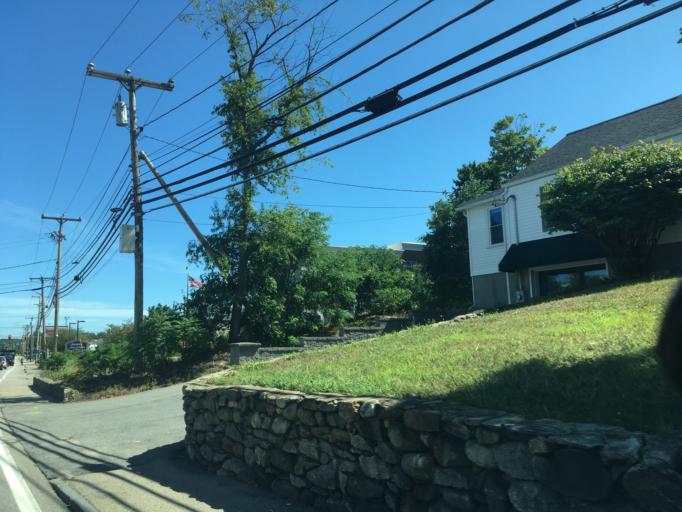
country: US
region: New Hampshire
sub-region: Rockingham County
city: Exeter
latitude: 42.9839
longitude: -70.9391
